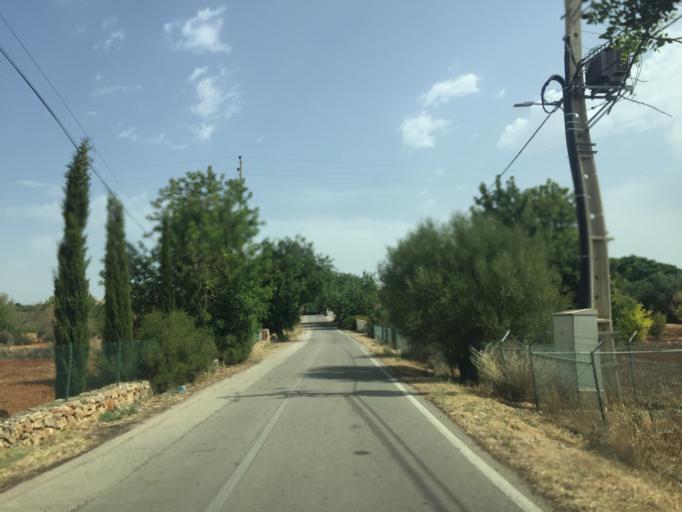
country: PT
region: Faro
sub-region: Loule
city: Boliqueime
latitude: 37.1245
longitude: -8.1440
